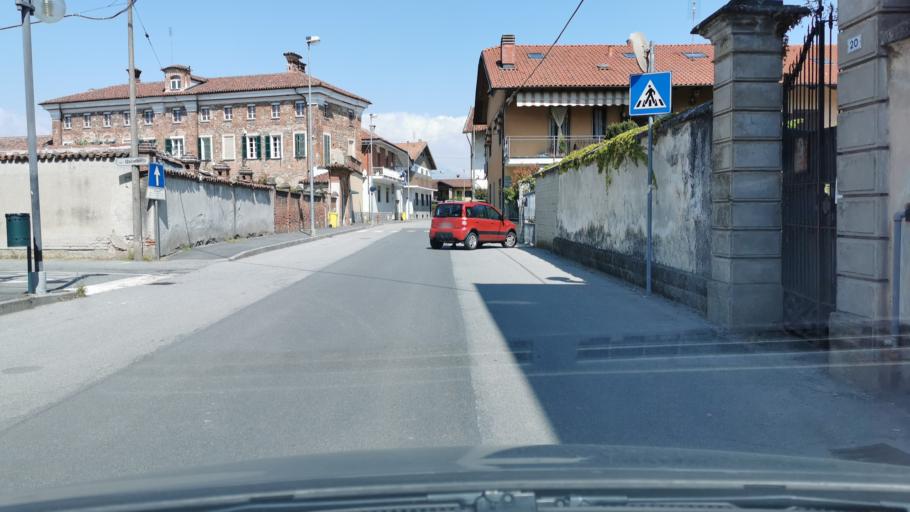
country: IT
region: Piedmont
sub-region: Provincia di Torino
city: Bosconero
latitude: 45.2695
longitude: 7.7645
